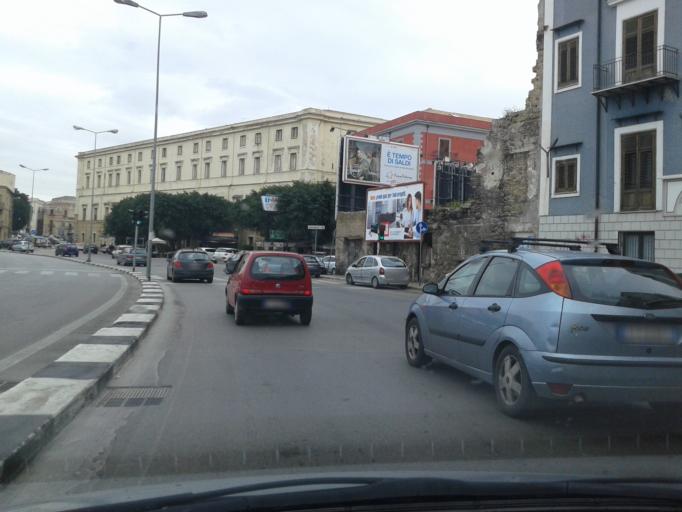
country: IT
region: Sicily
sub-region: Palermo
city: Palermo
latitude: 38.1195
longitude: 13.3666
